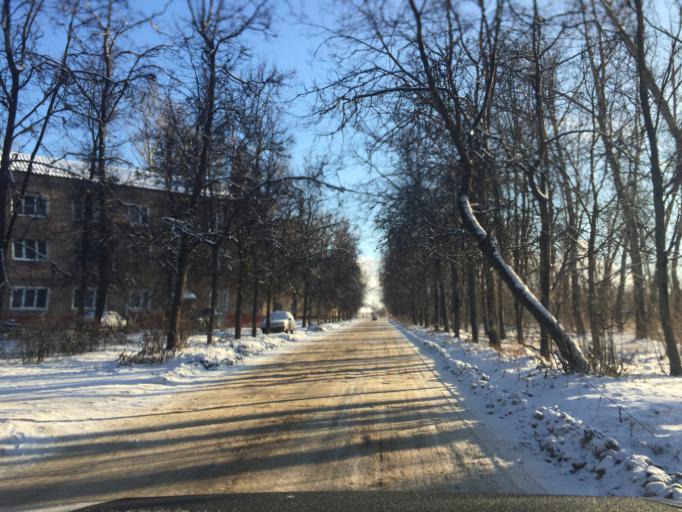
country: RU
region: Tula
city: Tula
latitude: 54.1795
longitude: 37.7022
